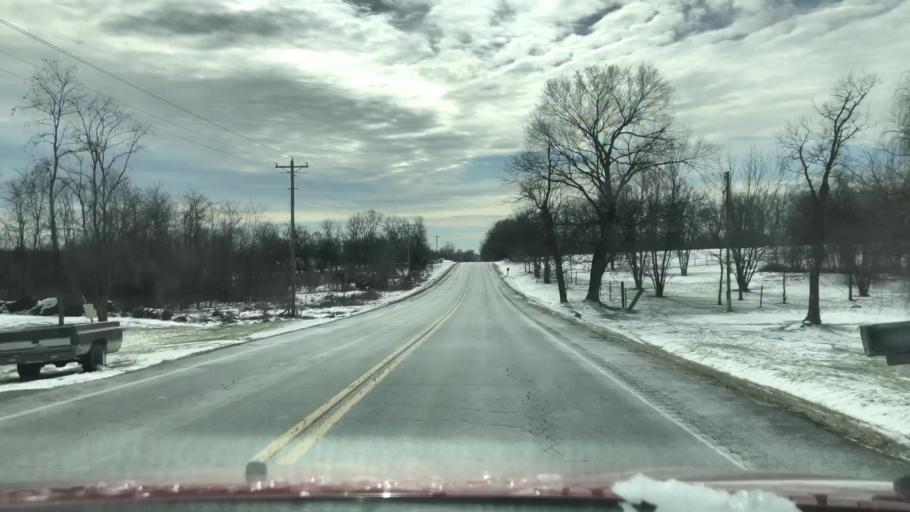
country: US
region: Missouri
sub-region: Jackson County
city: Lone Jack
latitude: 38.8801
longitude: -94.1351
